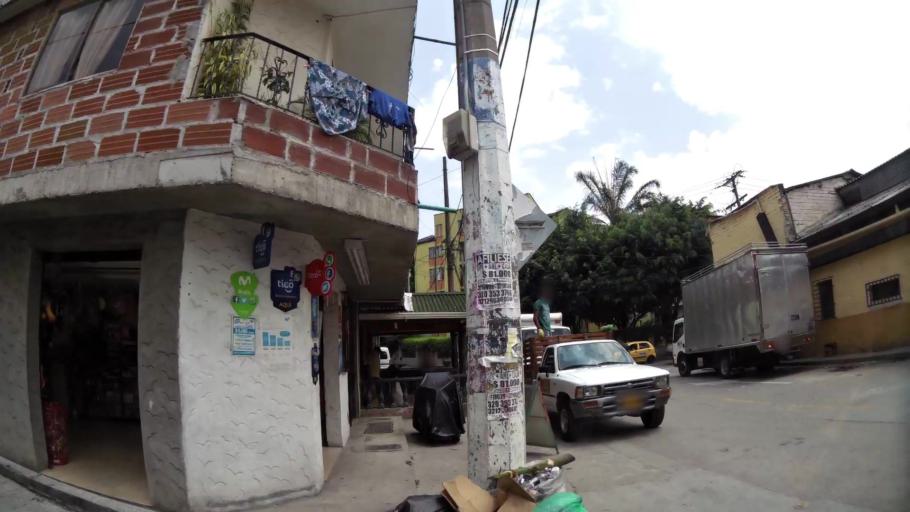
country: CO
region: Antioquia
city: Itagui
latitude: 6.1889
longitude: -75.5974
